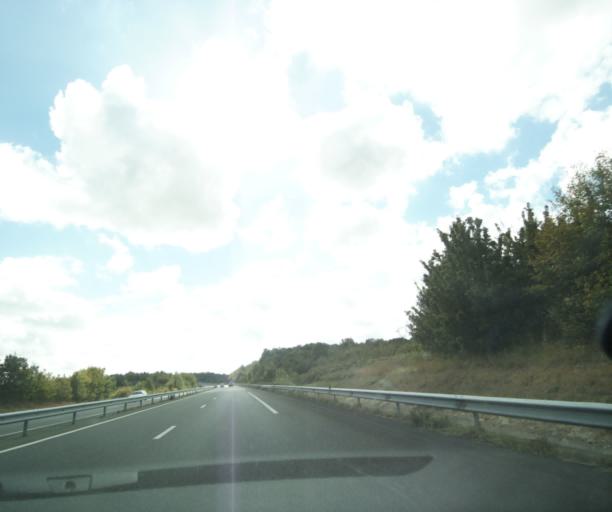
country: FR
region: Poitou-Charentes
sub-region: Departement de la Charente-Maritime
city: Saint-Georges-des-Coteaux
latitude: 45.8105
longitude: -0.6975
